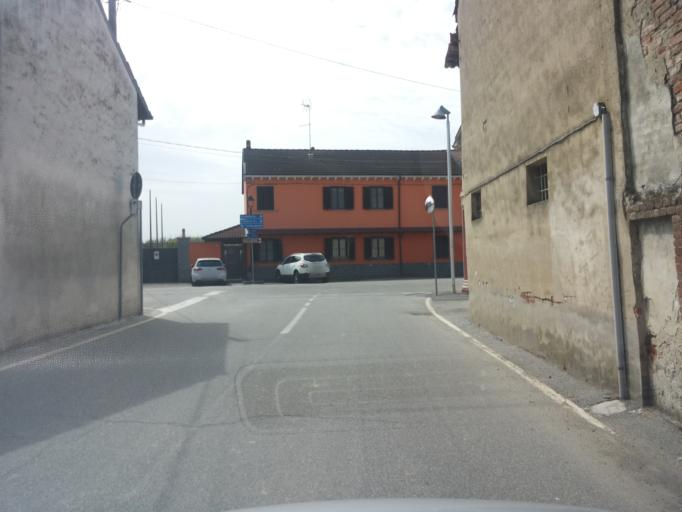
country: IT
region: Piedmont
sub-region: Provincia di Vercelli
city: Motta De Conti
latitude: 45.1916
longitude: 8.5179
